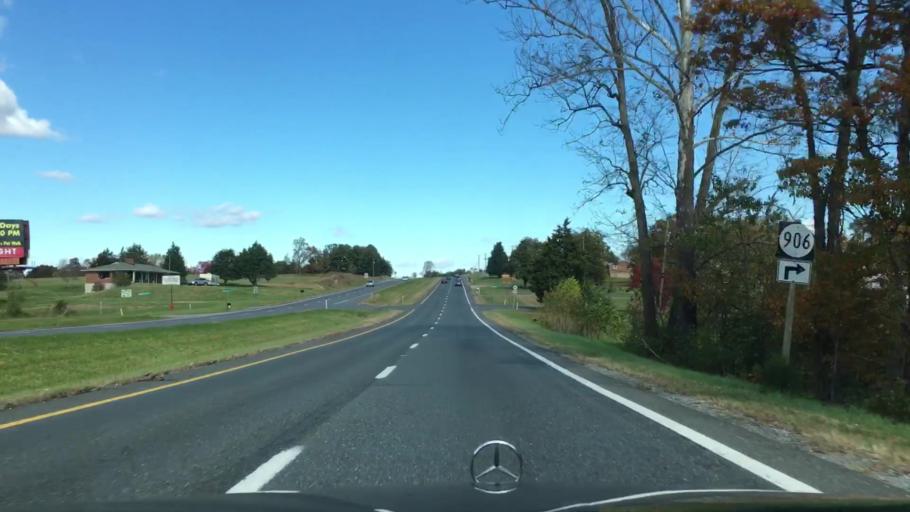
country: US
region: Virginia
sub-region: Campbell County
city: Altavista
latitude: 37.1809
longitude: -79.2048
